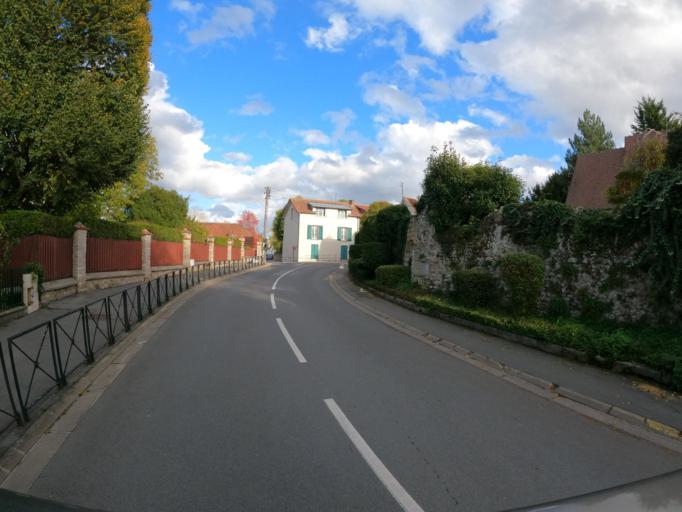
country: FR
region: Ile-de-France
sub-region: Departement de Seine-et-Marne
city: Chessy
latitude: 48.8799
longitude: 2.7619
